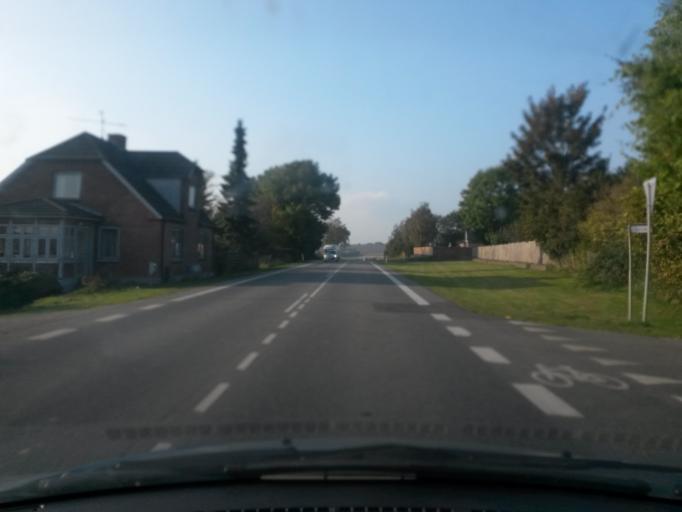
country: DK
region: Central Jutland
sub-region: Syddjurs Kommune
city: Hornslet
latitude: 56.3649
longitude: 10.3262
